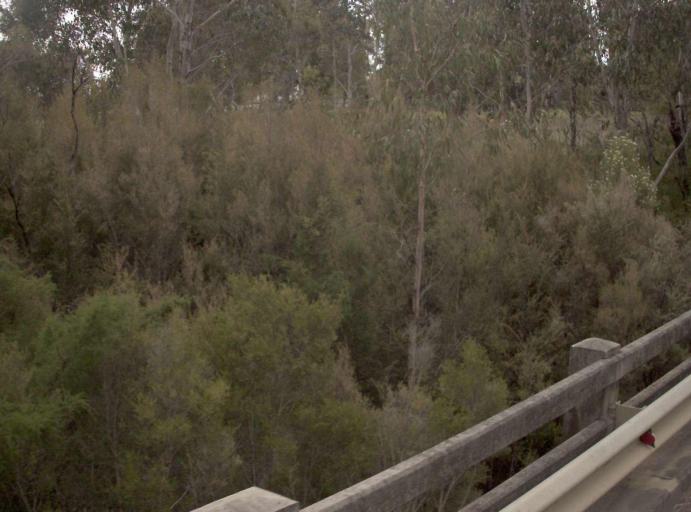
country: AU
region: Victoria
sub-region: Wellington
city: Sale
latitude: -38.3282
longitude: 147.0180
